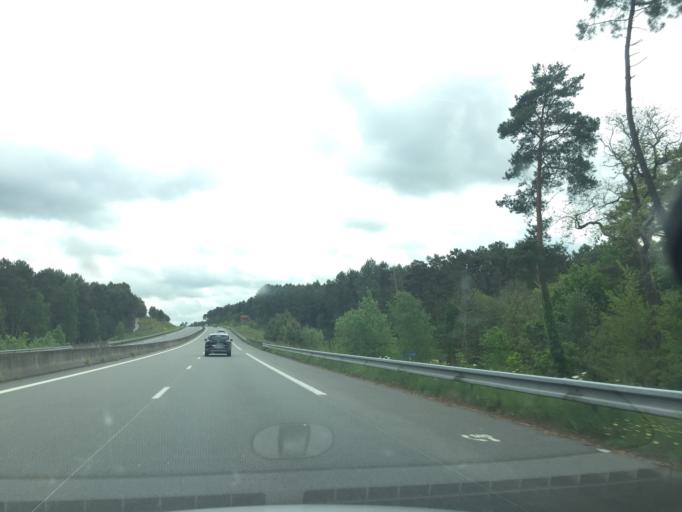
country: FR
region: Pays de la Loire
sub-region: Departement de la Sarthe
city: Mayet
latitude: 47.7579
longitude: 0.3145
